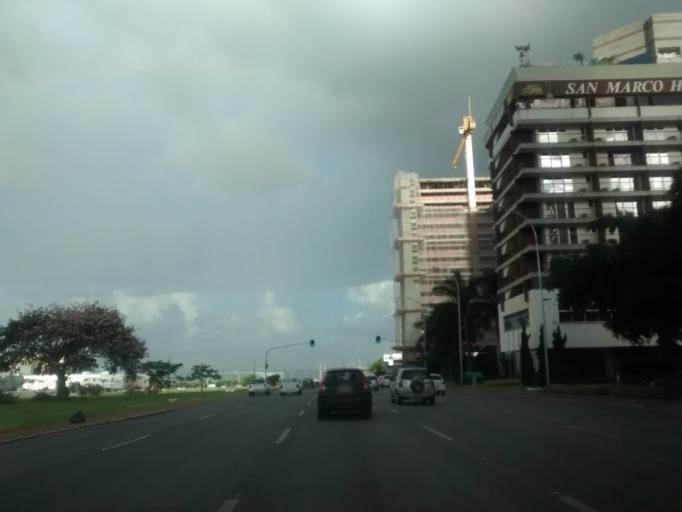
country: BR
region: Federal District
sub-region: Brasilia
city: Brasilia
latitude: -15.7925
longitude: -47.8922
